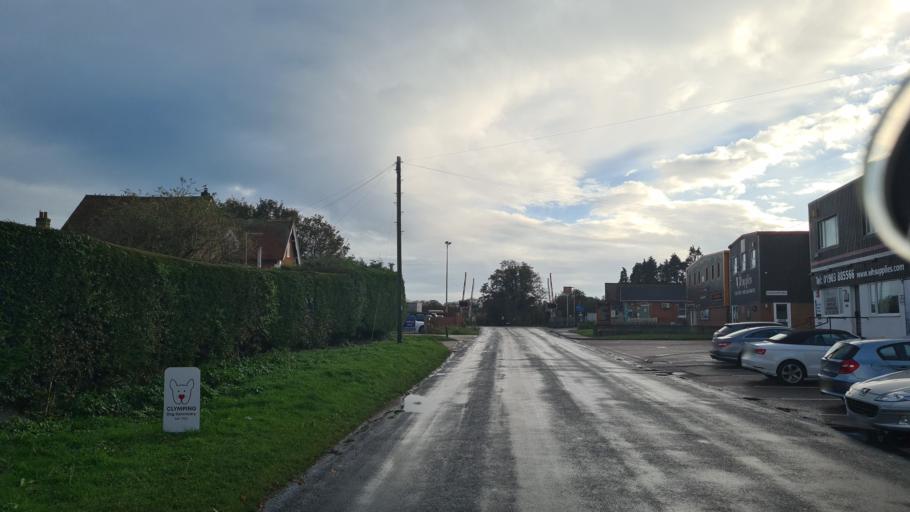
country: GB
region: England
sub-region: West Sussex
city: Arundel
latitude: 50.8301
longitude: -0.5772
